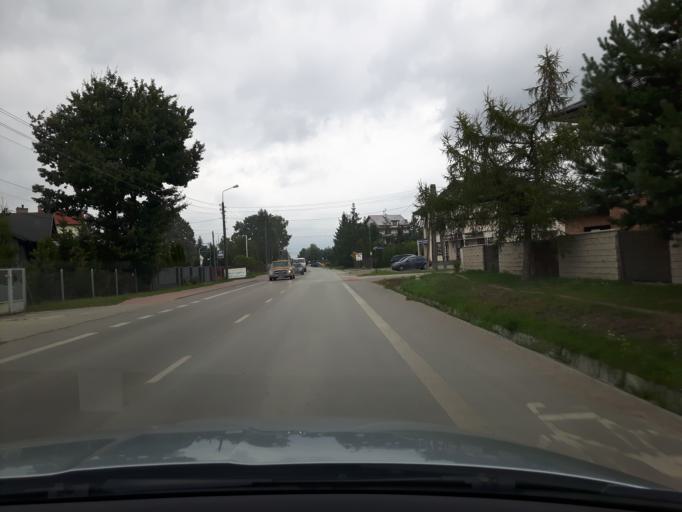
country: PL
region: Masovian Voivodeship
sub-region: Powiat wolominski
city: Kobylka
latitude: 52.3182
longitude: 21.1886
